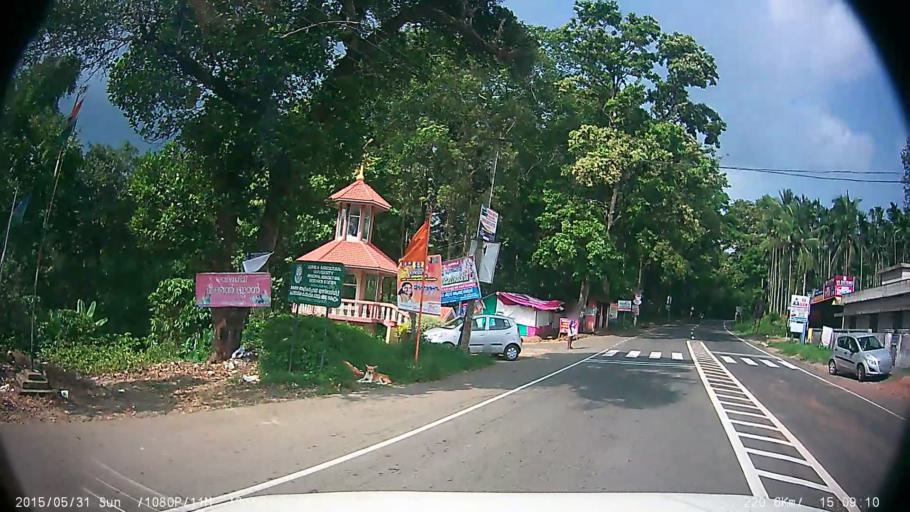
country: IN
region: Kerala
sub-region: Wayanad
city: Panamaram
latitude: 11.6543
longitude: 76.2168
